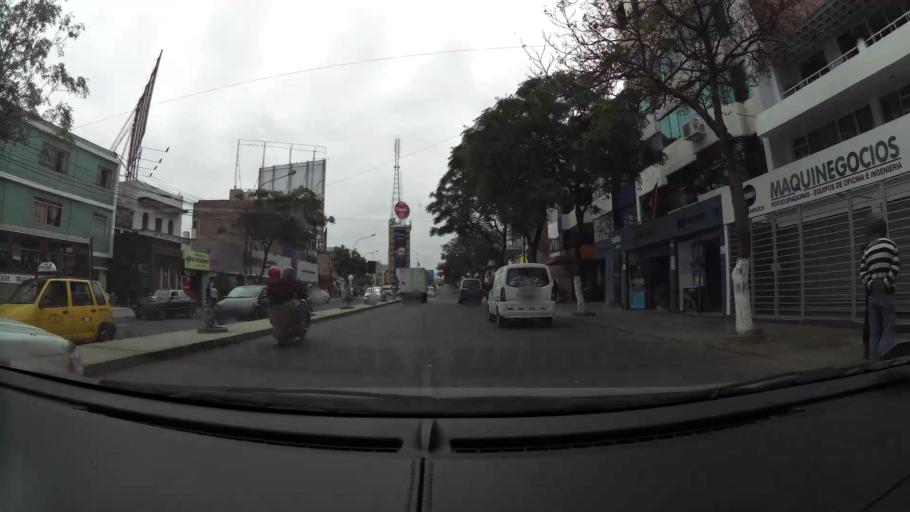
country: PE
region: La Libertad
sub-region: Provincia de Trujillo
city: Trujillo
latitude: -8.1152
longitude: -79.0314
